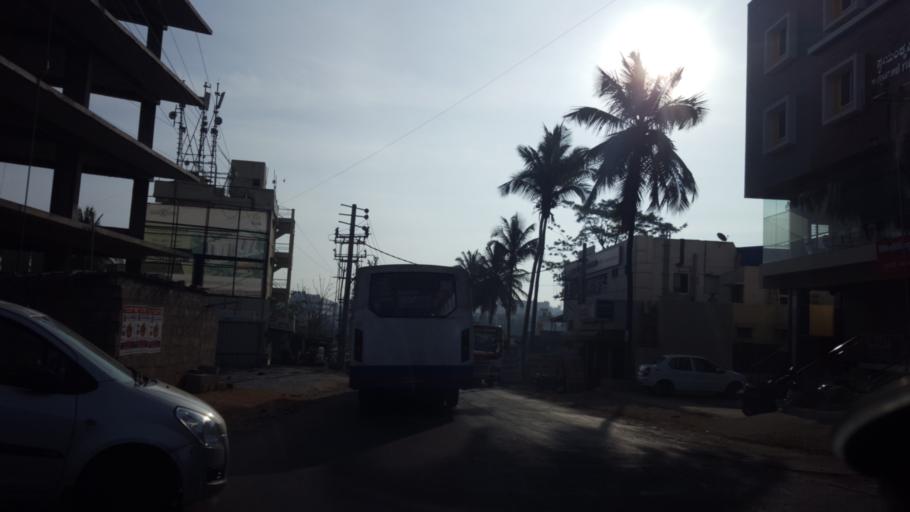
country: IN
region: Karnataka
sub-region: Bangalore Urban
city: Bangalore
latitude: 12.9039
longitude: 77.5087
